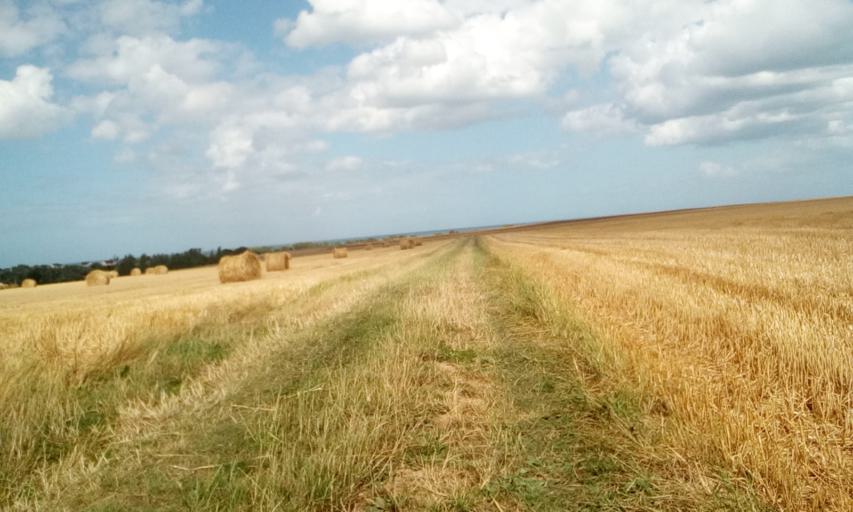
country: FR
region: Lower Normandy
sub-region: Departement du Calvados
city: Ver-sur-Mer
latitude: 49.3303
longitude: -0.5198
